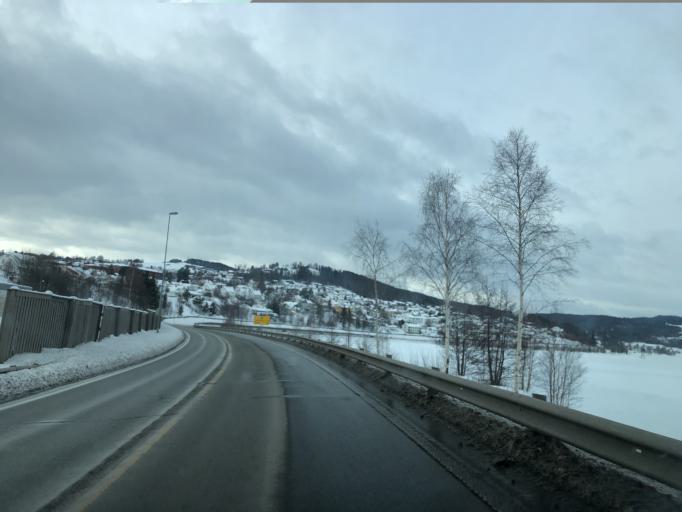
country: NO
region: Oppland
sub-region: Gjovik
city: Gjovik
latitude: 60.8008
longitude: 10.6933
